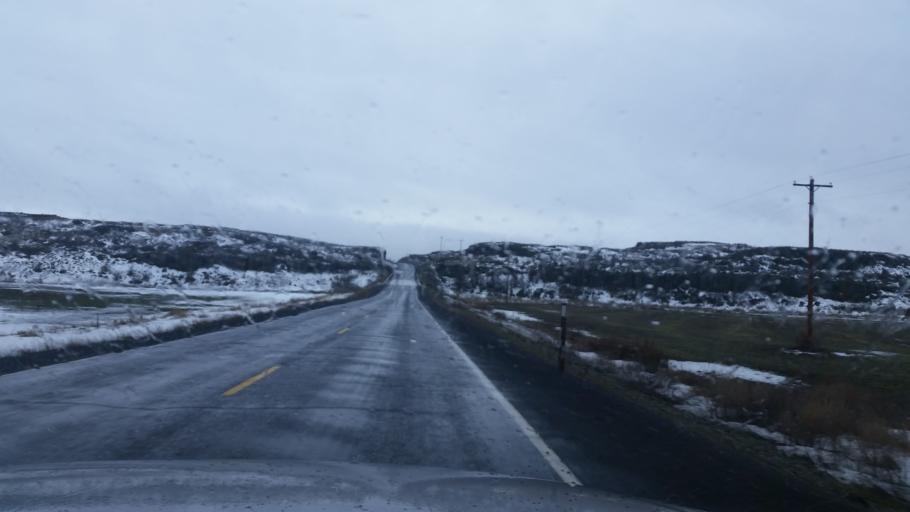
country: US
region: Washington
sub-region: Lincoln County
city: Davenport
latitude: 47.3620
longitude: -118.1094
